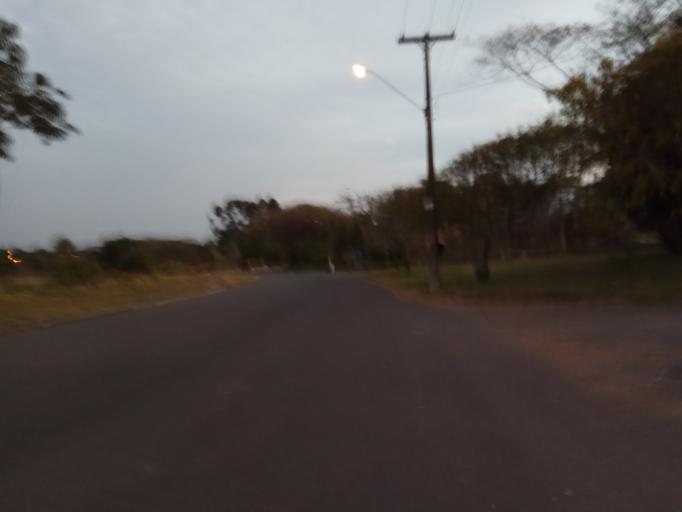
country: BR
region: Sao Paulo
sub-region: Piracicaba
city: Piracicaba
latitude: -22.7557
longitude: -47.5886
